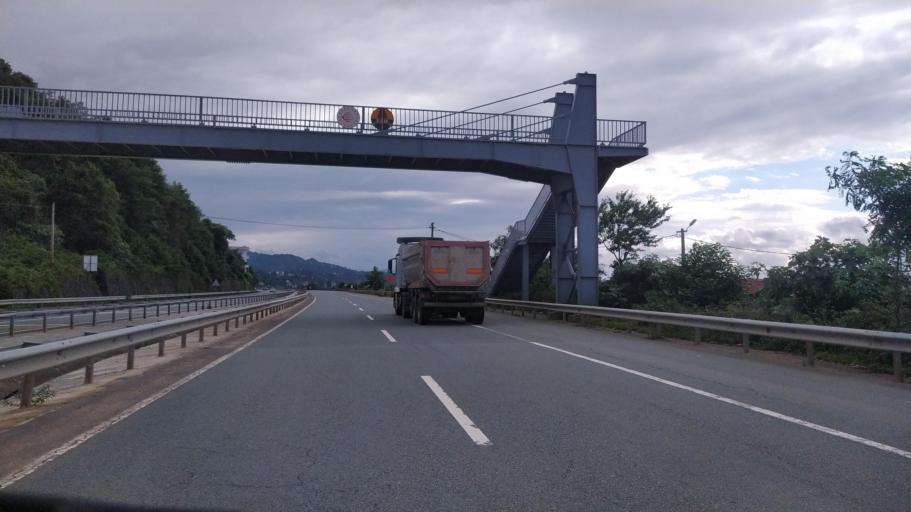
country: TR
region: Rize
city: Findikli
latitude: 41.2307
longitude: 41.0812
